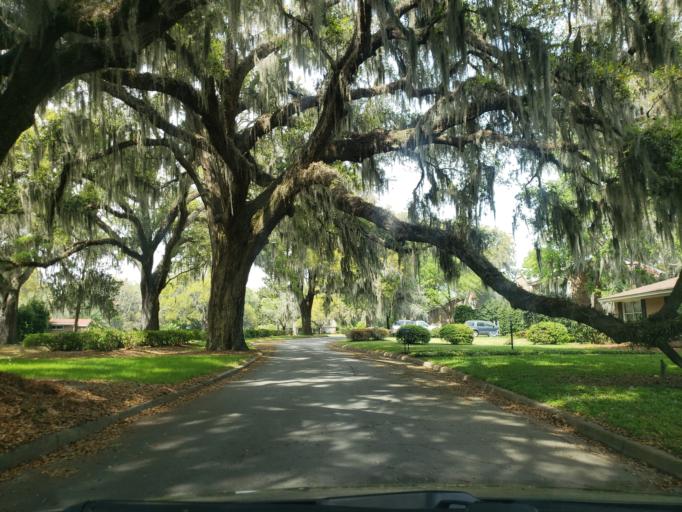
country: US
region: Georgia
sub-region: Chatham County
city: Isle of Hope
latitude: 31.9929
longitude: -81.0960
